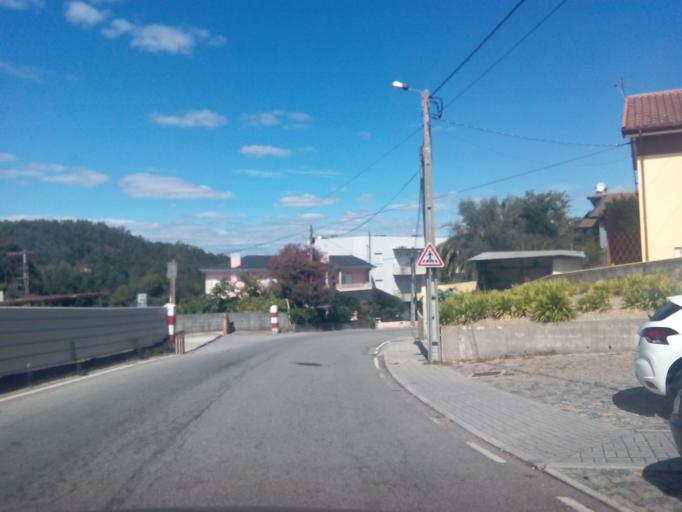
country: PT
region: Porto
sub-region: Paredes
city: Casteloes de Cepeda
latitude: 41.1559
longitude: -8.3163
